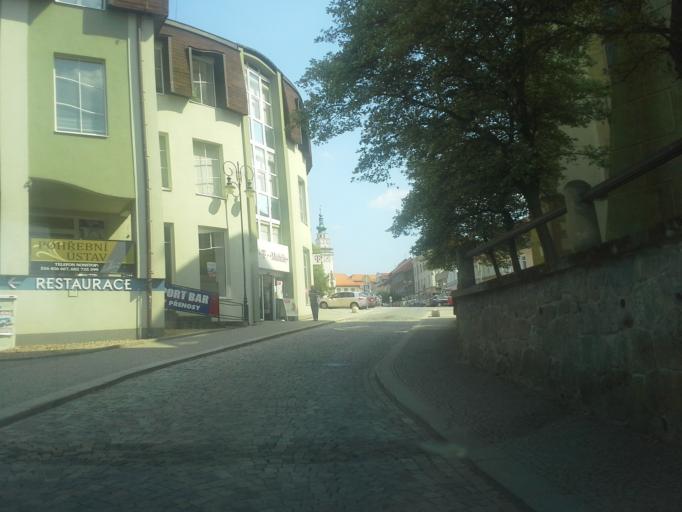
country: CZ
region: South Moravian
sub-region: Okres Blansko
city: Boskovice
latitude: 49.4887
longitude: 16.6587
